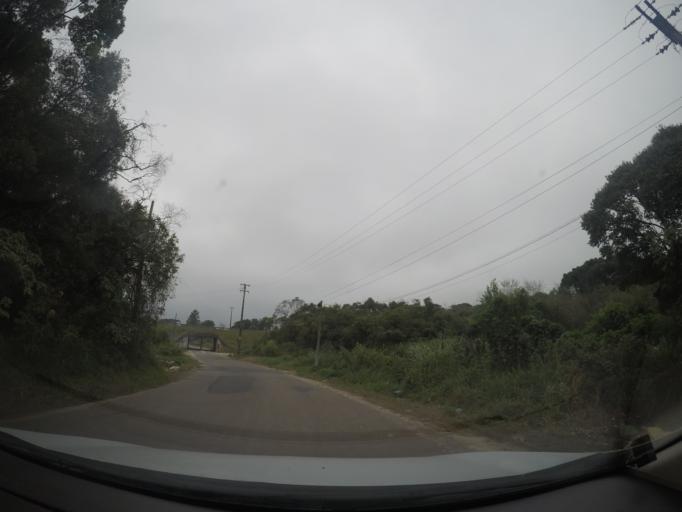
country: BR
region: Parana
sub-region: Colombo
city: Colombo
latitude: -25.3337
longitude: -49.2529
